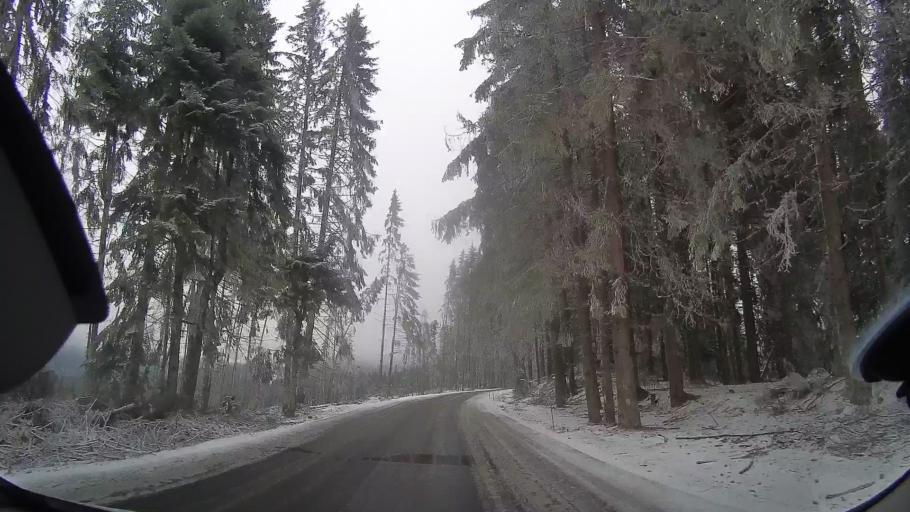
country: RO
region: Cluj
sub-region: Comuna Belis
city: Belis
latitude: 46.6450
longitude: 23.0425
